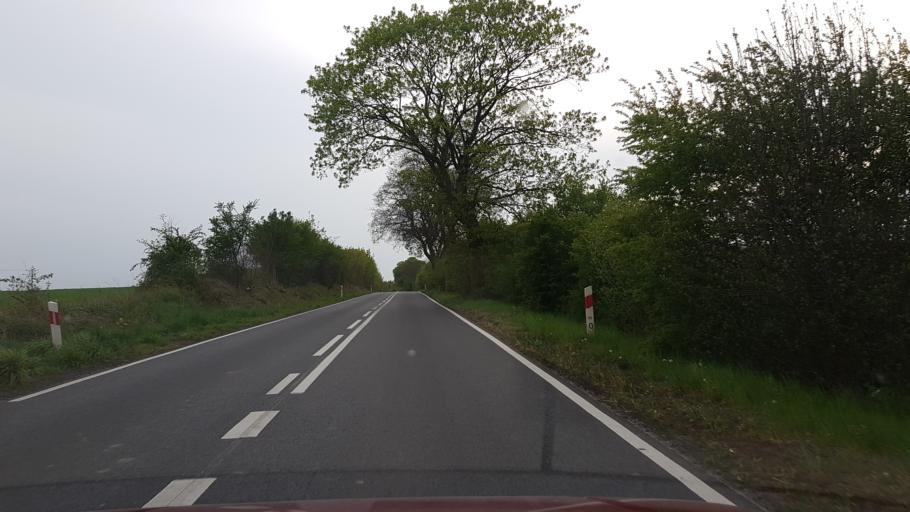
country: PL
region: West Pomeranian Voivodeship
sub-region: Powiat gryfinski
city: Stare Czarnowo
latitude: 53.2869
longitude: 14.7148
